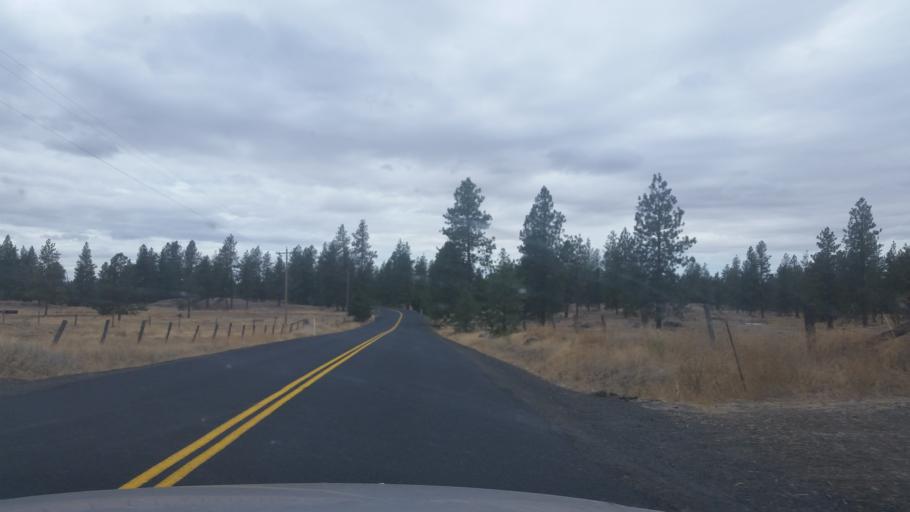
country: US
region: Washington
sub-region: Spokane County
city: Medical Lake
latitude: 47.5165
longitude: -117.7477
